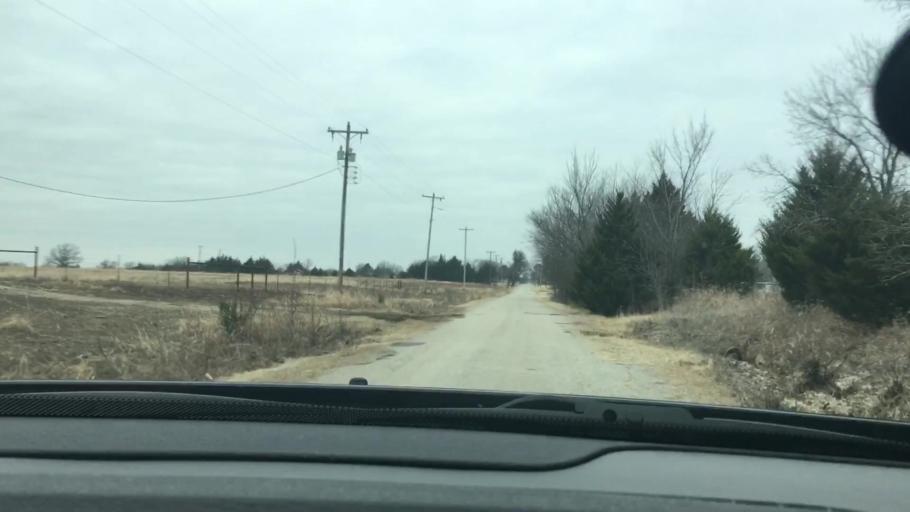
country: US
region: Oklahoma
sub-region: Carter County
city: Healdton
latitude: 34.2165
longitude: -97.4629
